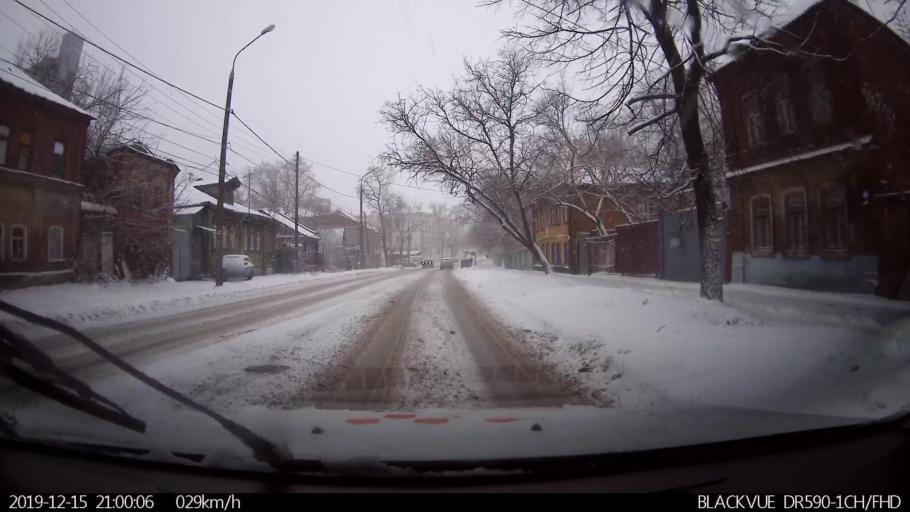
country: RU
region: Nizjnij Novgorod
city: Nizhniy Novgorod
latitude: 56.3154
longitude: 43.9520
